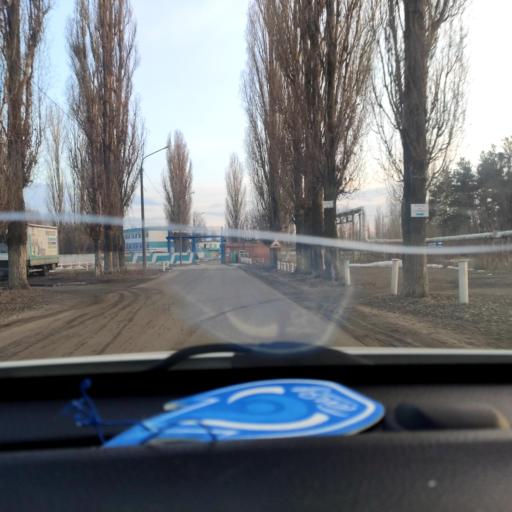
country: RU
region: Voronezj
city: Maslovka
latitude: 51.5984
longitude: 39.2207
